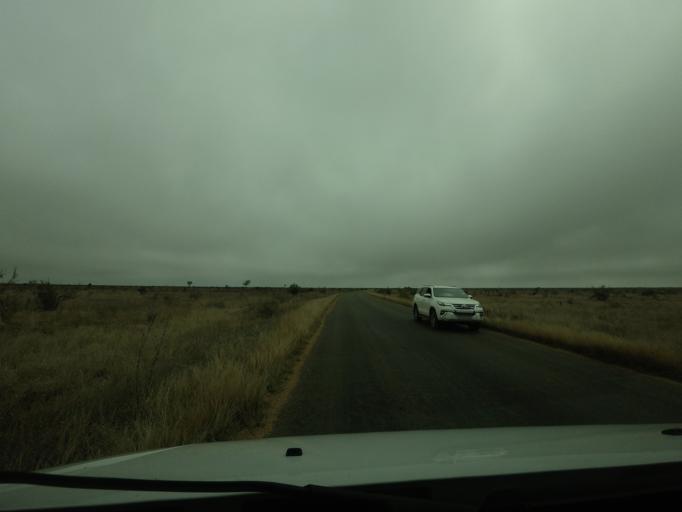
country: ZA
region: Limpopo
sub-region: Mopani District Municipality
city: Phalaborwa
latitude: -24.2370
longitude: 31.7198
